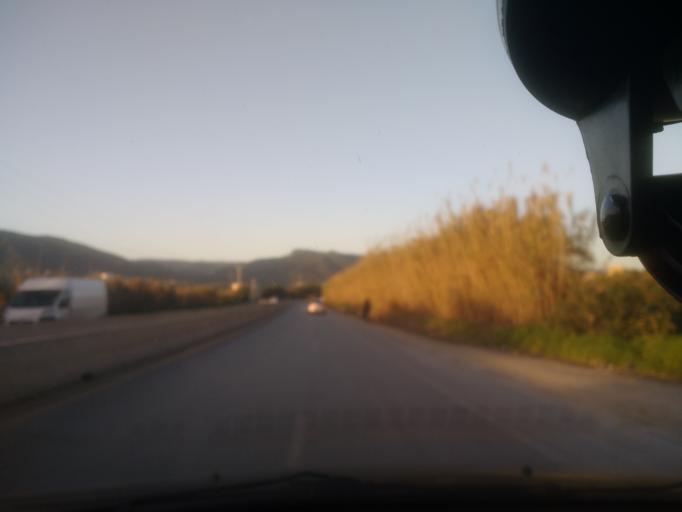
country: DZ
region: Tizi Ouzou
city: Tizi Ouzou
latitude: 36.7487
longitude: 4.0152
